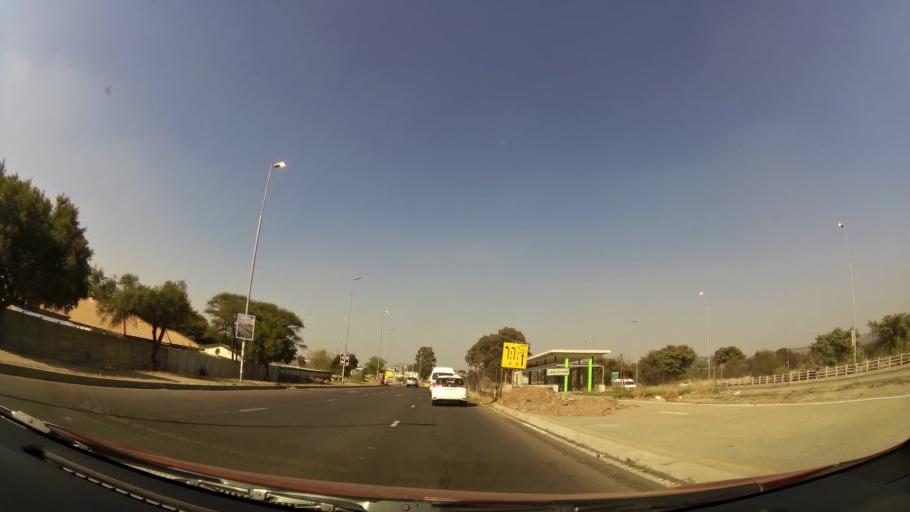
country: ZA
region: North-West
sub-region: Bojanala Platinum District Municipality
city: Rustenburg
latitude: -25.6606
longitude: 27.2296
